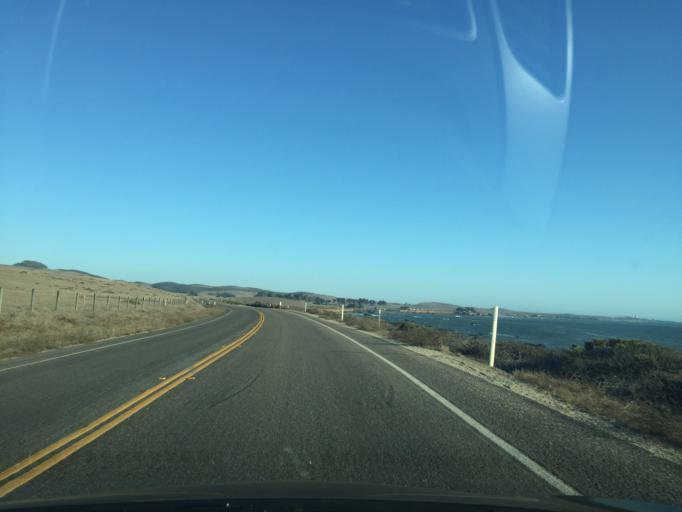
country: US
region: California
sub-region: San Luis Obispo County
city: Cambria
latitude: 35.7006
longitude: -121.3012
